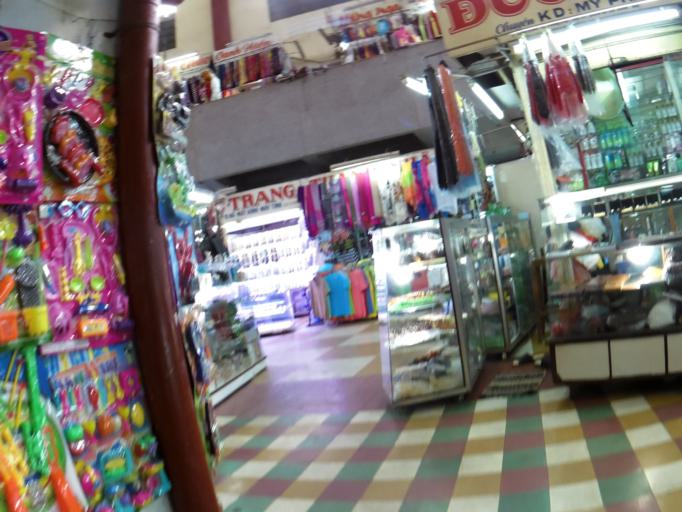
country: VN
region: Khanh Hoa
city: Nha Trang
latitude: 12.2549
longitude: 109.1913
